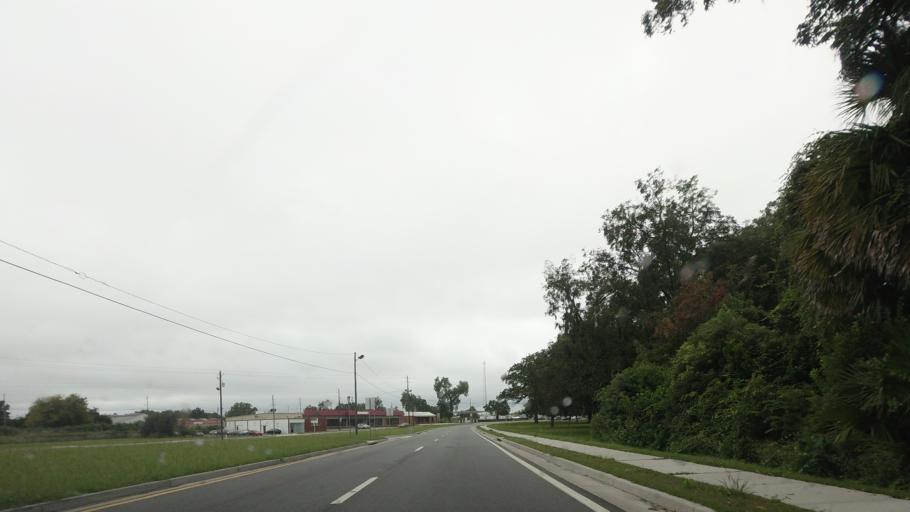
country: US
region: Georgia
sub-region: Lowndes County
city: Valdosta
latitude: 30.8297
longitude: -83.2841
